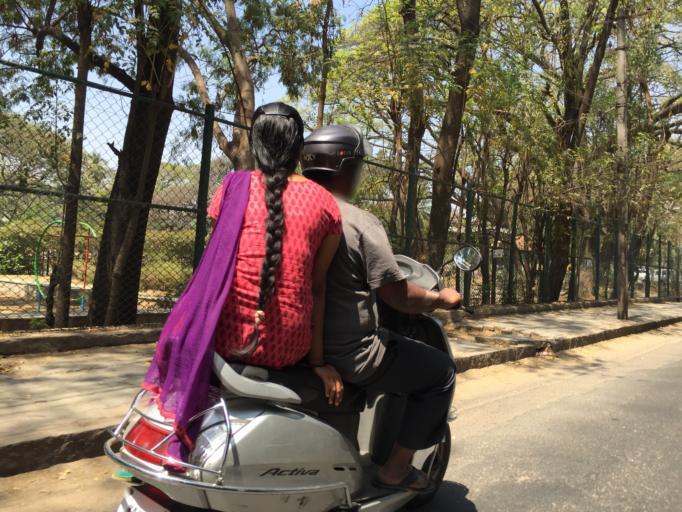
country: IN
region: Karnataka
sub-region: Bangalore Urban
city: Bangalore
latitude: 12.9868
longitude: 77.6225
